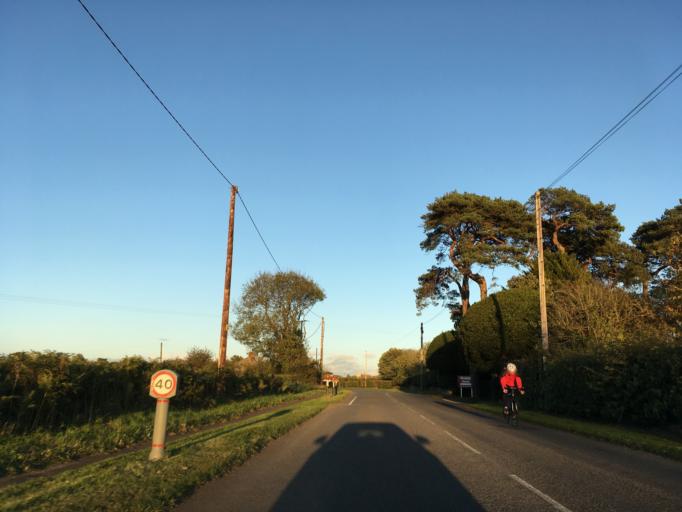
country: GB
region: England
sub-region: South Gloucestershire
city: Alveston
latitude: 51.5835
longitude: -2.5591
